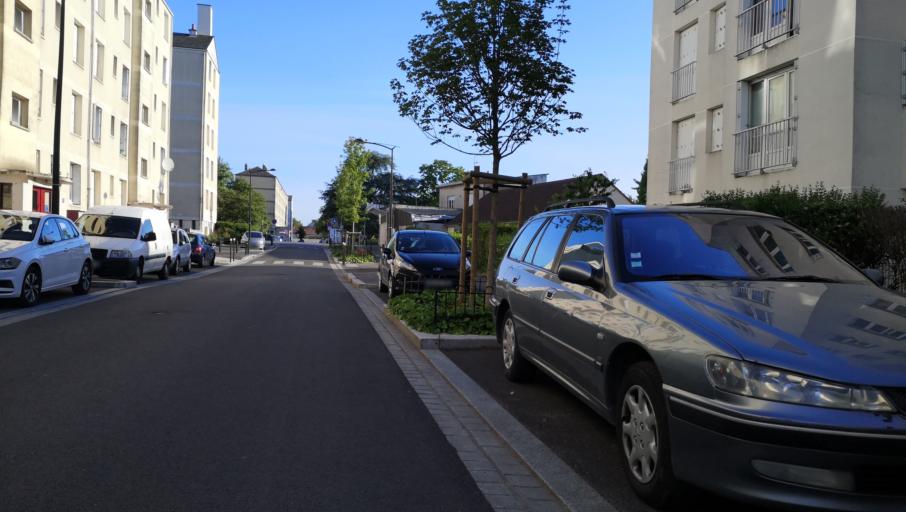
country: FR
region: Centre
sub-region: Departement du Loiret
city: Semoy
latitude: 47.9137
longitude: 1.9353
